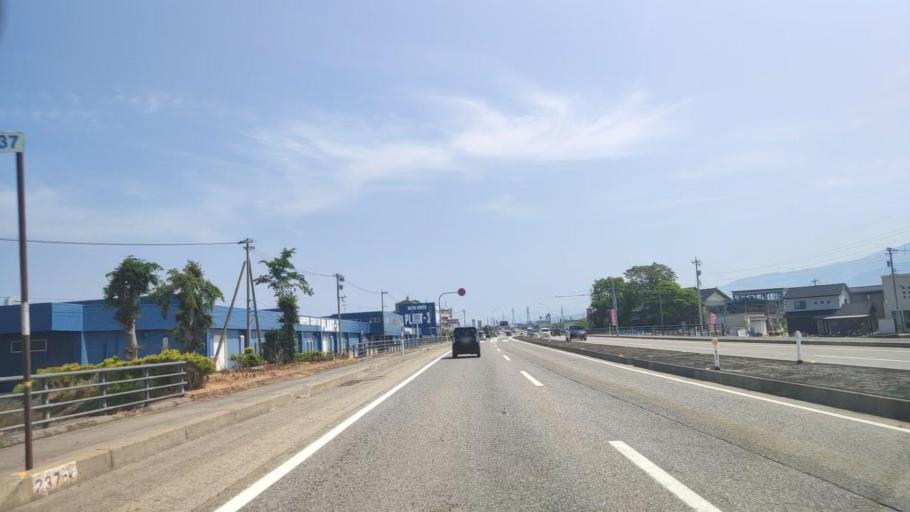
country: JP
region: Toyama
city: Namerikawa
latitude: 36.7495
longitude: 137.3511
